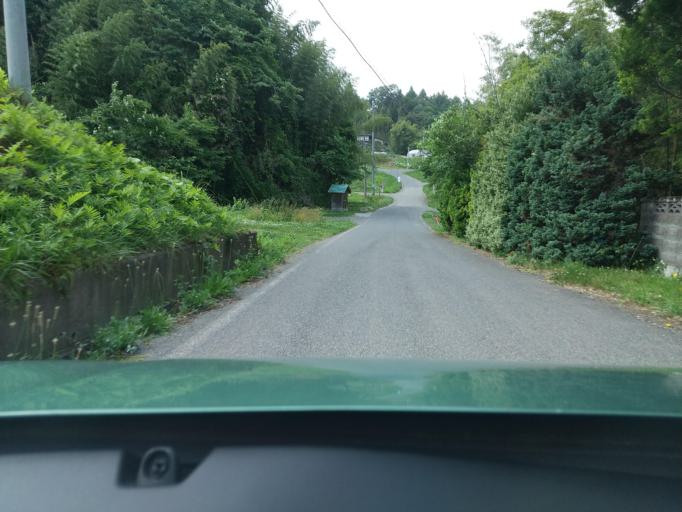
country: JP
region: Iwate
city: Ichinoseki
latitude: 39.0055
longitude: 141.2182
